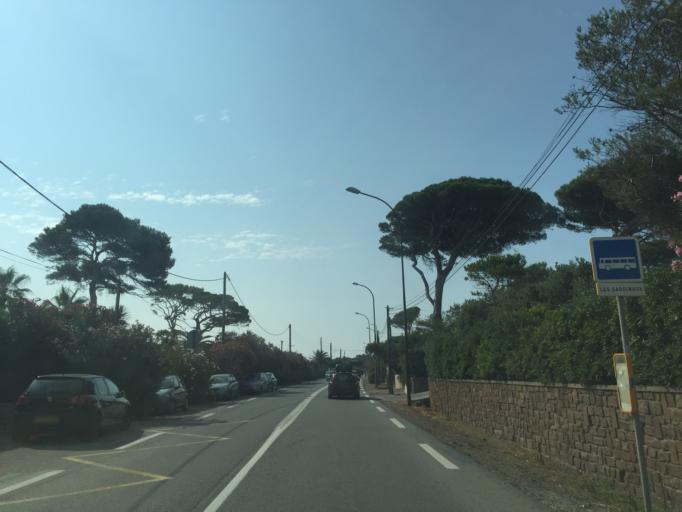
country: FR
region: Provence-Alpes-Cote d'Azur
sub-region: Departement du Var
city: Sainte-Maxime
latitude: 43.3166
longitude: 6.6670
